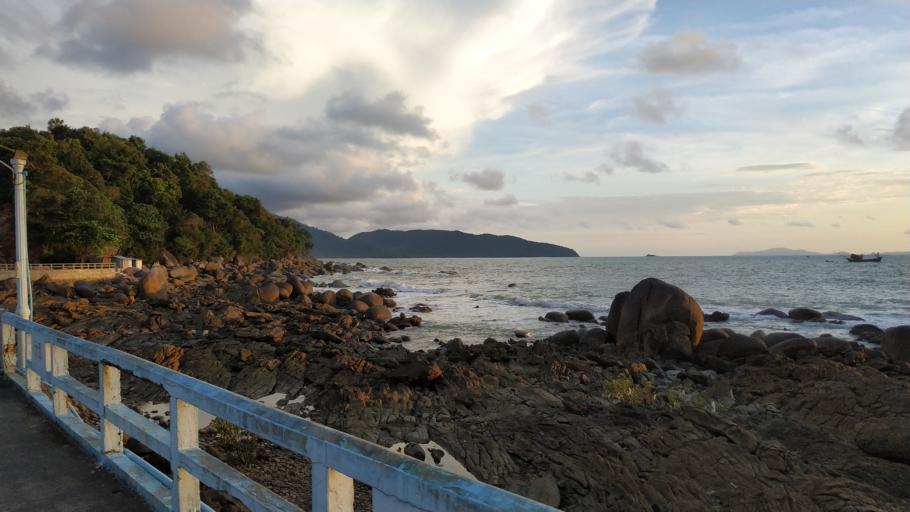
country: MM
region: Tanintharyi
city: Dawei
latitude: 14.0868
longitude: 98.0706
